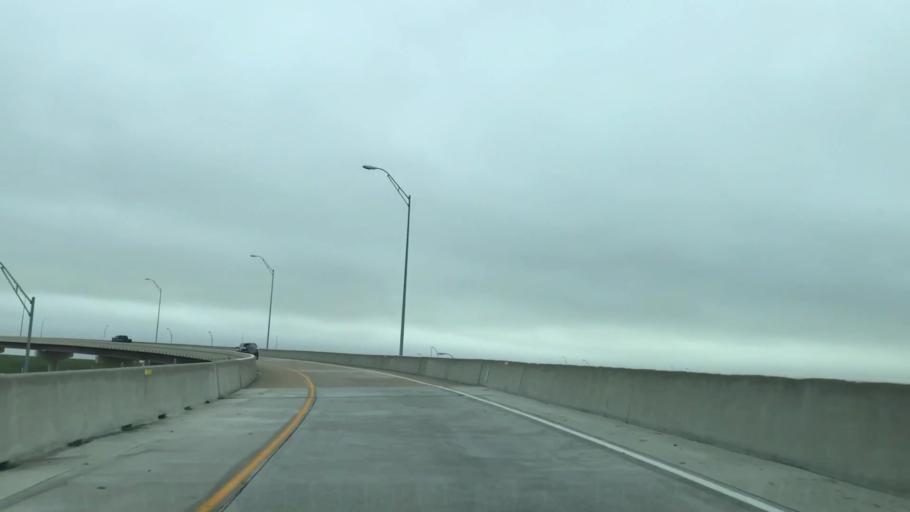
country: US
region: Texas
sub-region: Dallas County
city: Coppell
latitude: 32.9341
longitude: -97.0371
